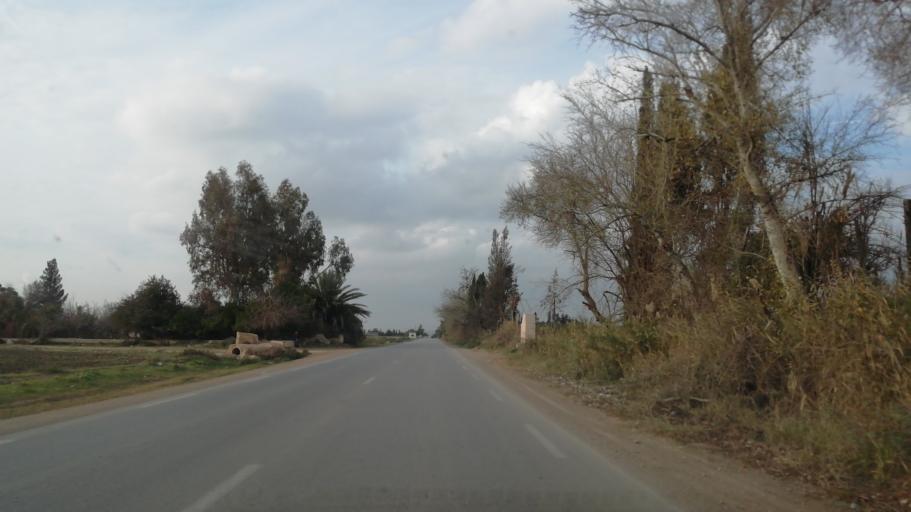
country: DZ
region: Mascara
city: Sig
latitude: 35.6819
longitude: -0.0113
